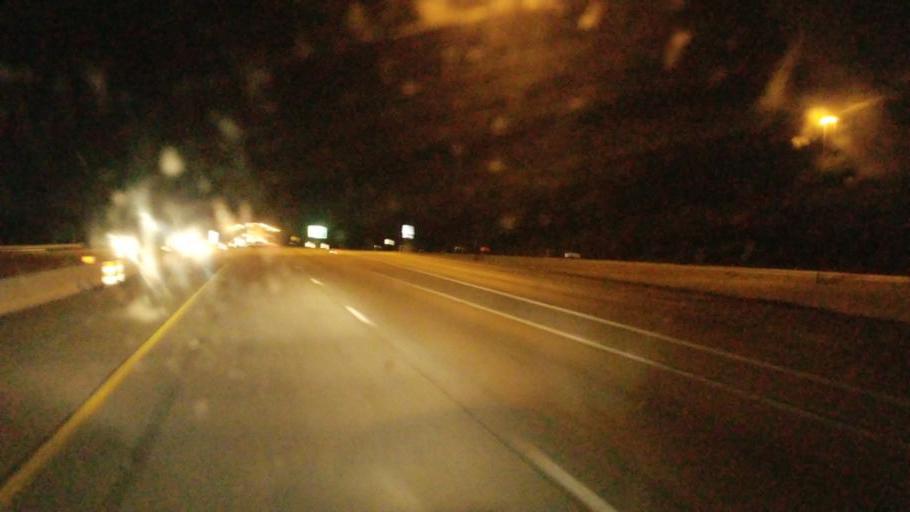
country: US
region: Indiana
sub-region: Allen County
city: New Haven
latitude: 41.0847
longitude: -84.9929
